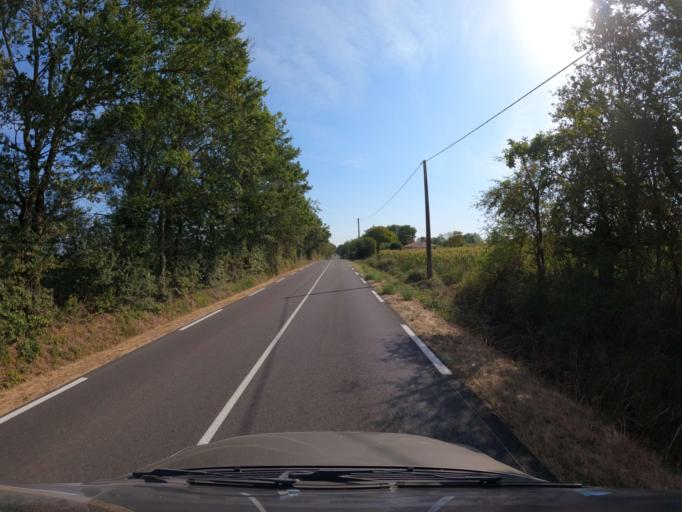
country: FR
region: Pays de la Loire
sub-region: Departement de la Vendee
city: Saint-Christophe-du-Ligneron
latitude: 46.8007
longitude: -1.7891
